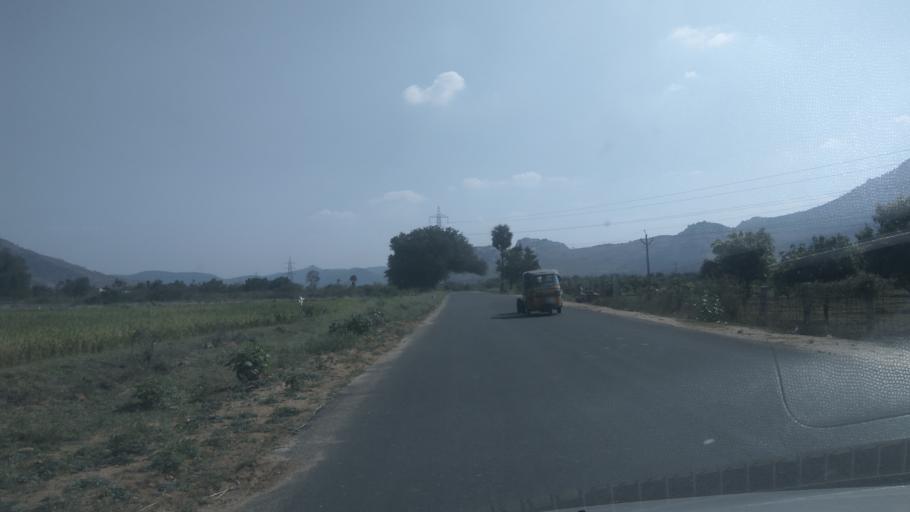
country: IN
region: Andhra Pradesh
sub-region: Chittoor
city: Renigunta
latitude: 13.5498
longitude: 79.4822
